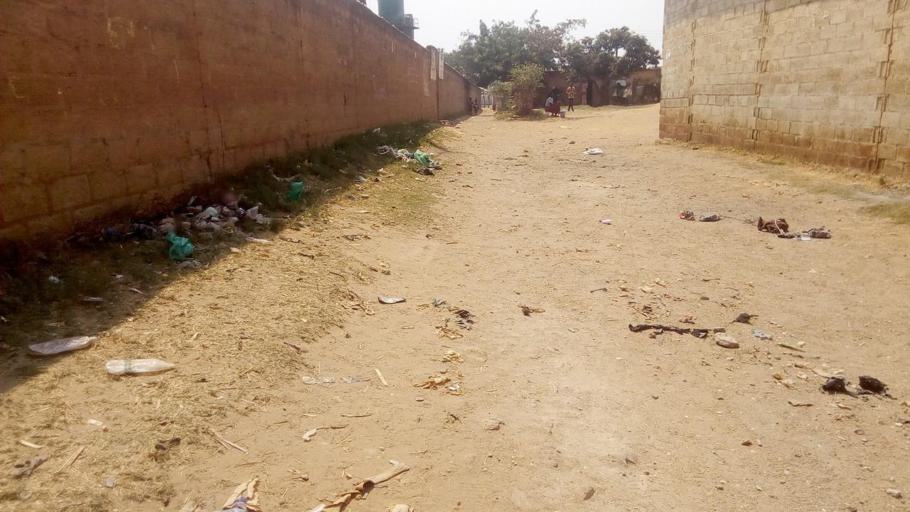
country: ZM
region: Lusaka
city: Lusaka
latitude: -15.3605
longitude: 28.2945
